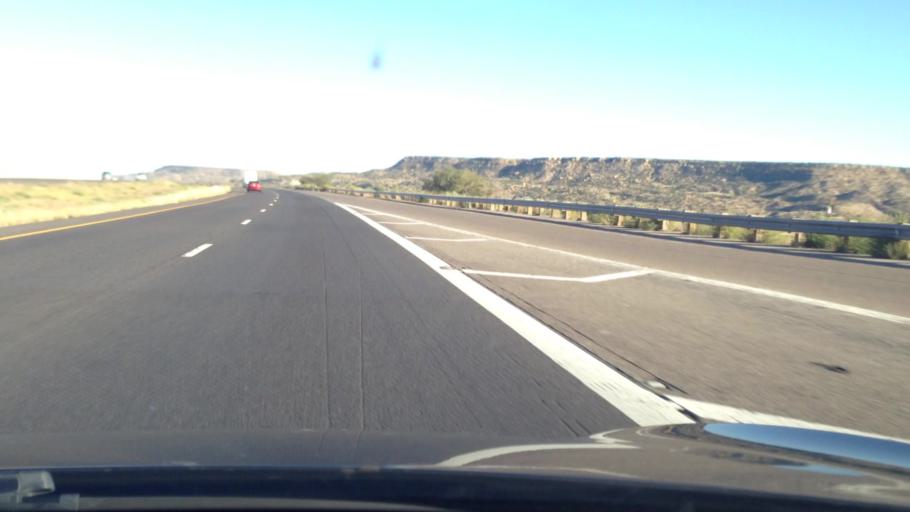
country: US
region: New Mexico
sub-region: Cibola County
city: Skyline-Ganipa
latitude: 35.0541
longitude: -107.5197
